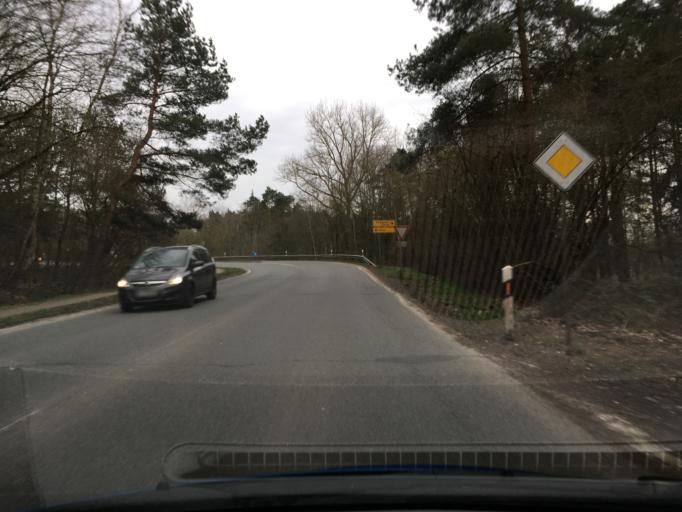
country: DE
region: Lower Saxony
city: Uelzen
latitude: 52.9902
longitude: 10.5683
